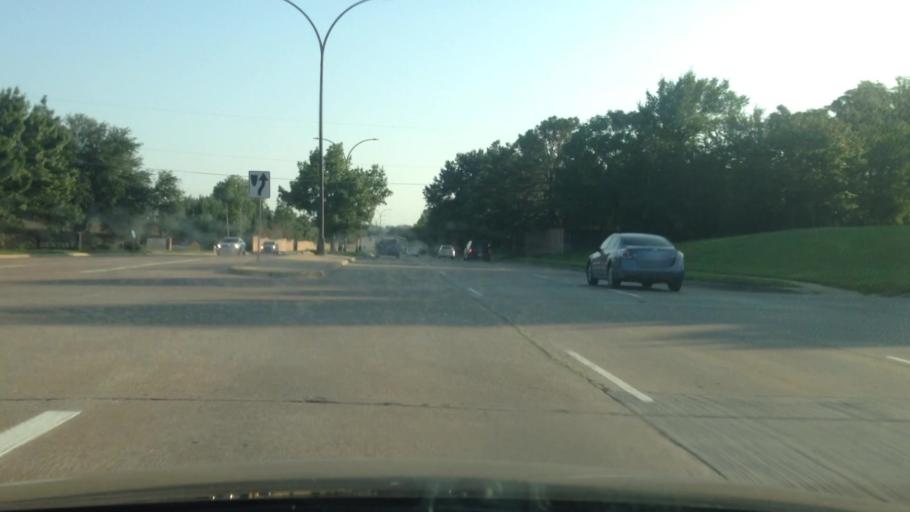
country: US
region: Texas
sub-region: Tarrant County
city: Dalworthington Gardens
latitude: 32.6890
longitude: -97.1920
